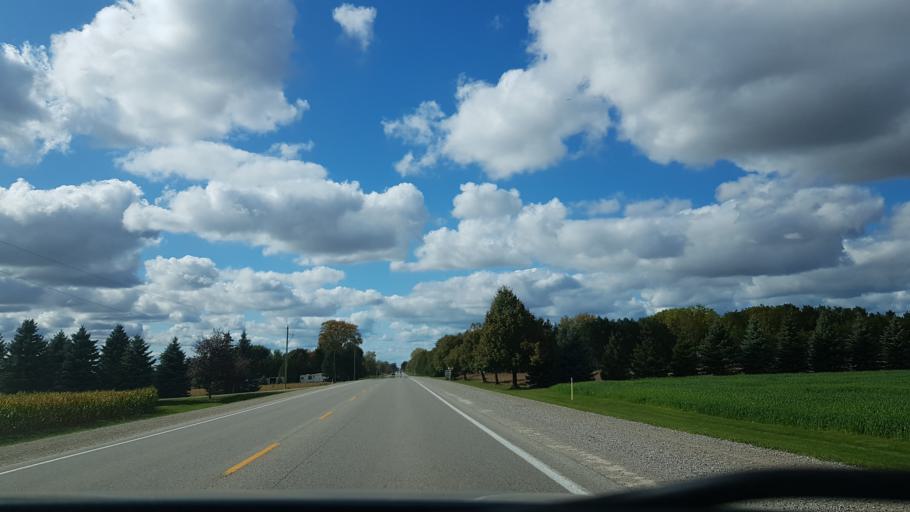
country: CA
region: Ontario
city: South Huron
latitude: 43.3579
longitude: -81.5204
